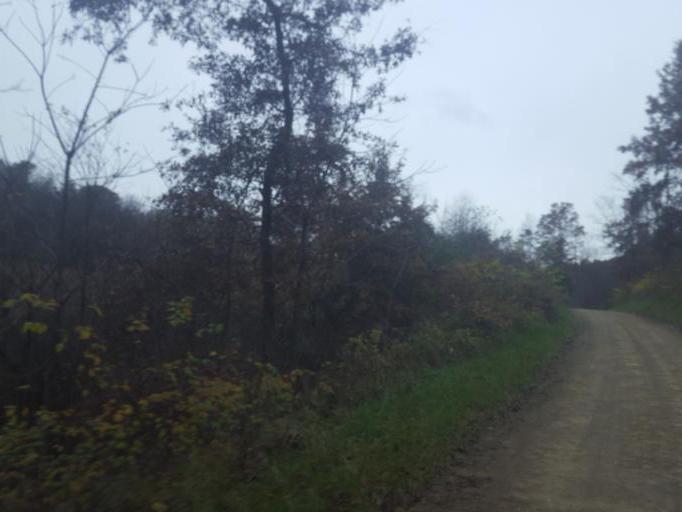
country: US
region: Ohio
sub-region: Knox County
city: Oak Hill
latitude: 40.4653
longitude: -82.0955
